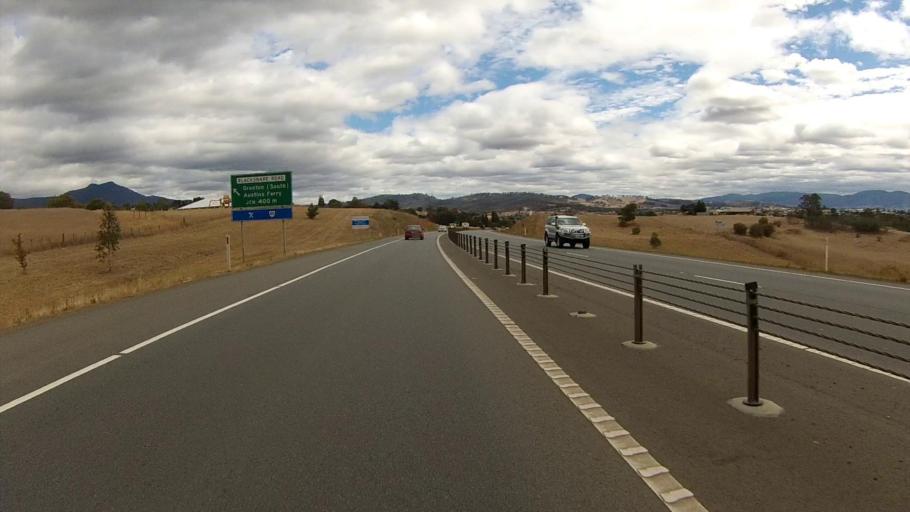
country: AU
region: Tasmania
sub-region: Glenorchy
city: Granton
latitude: -42.7590
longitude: 147.2316
